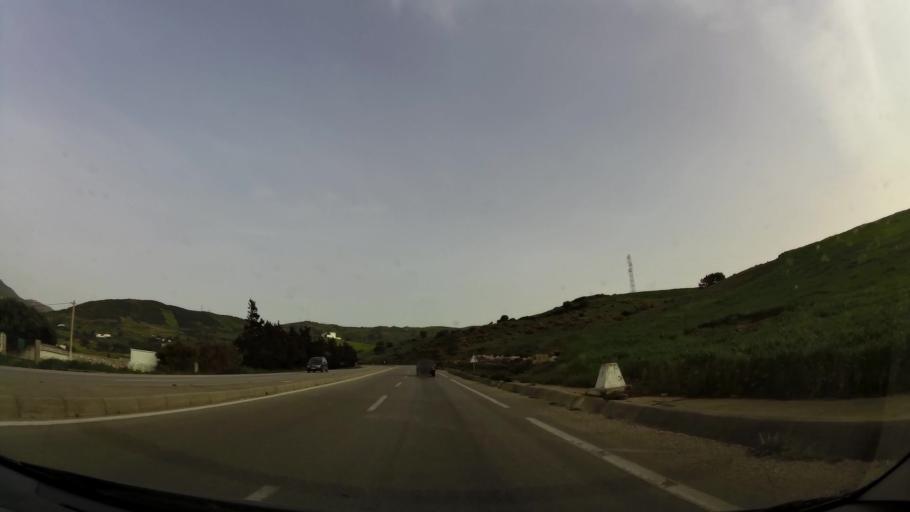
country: MA
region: Tanger-Tetouan
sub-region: Tanger-Assilah
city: Dar Chaoui
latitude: 35.5650
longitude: -5.6063
